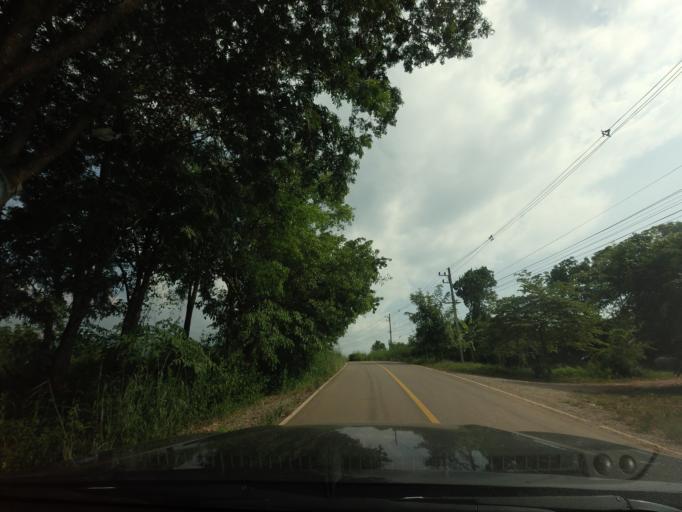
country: TH
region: Phitsanulok
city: Nakhon Thai
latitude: 17.0445
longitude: 100.9107
